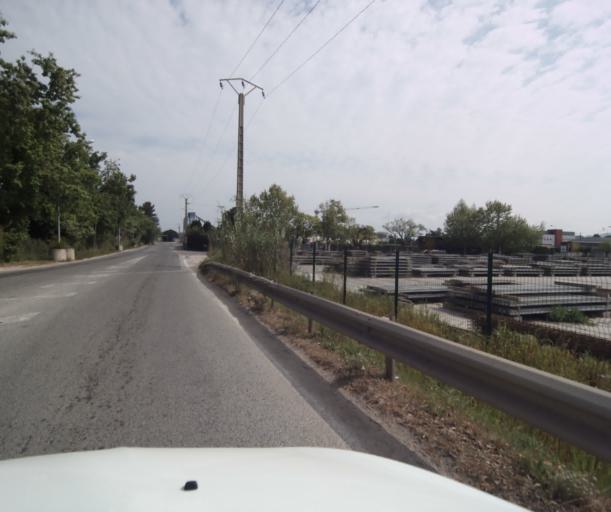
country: FR
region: Provence-Alpes-Cote d'Azur
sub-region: Departement du Var
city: La Farlede
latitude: 43.1412
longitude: 6.0302
